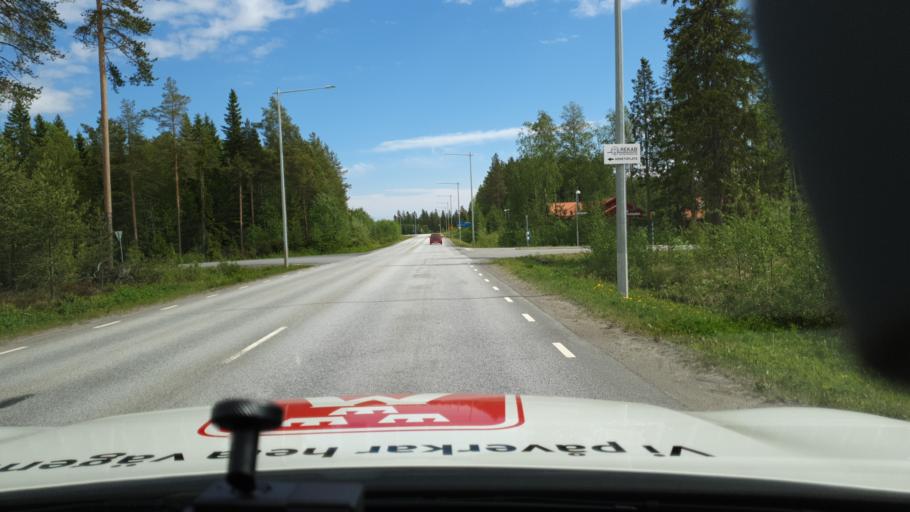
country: SE
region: Vaesterbotten
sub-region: Umea Kommun
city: Ersmark
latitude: 63.8024
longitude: 20.3543
